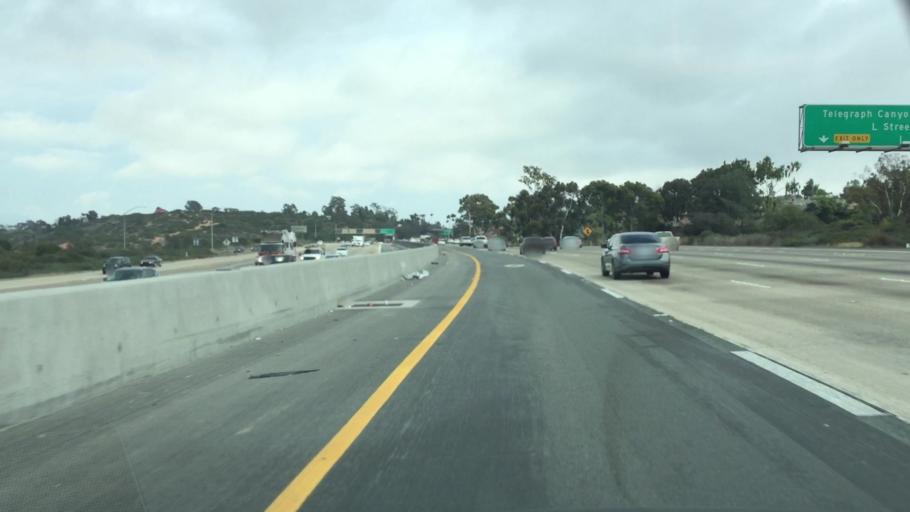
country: US
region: California
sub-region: San Diego County
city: Chula Vista
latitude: 32.6398
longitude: -117.0547
